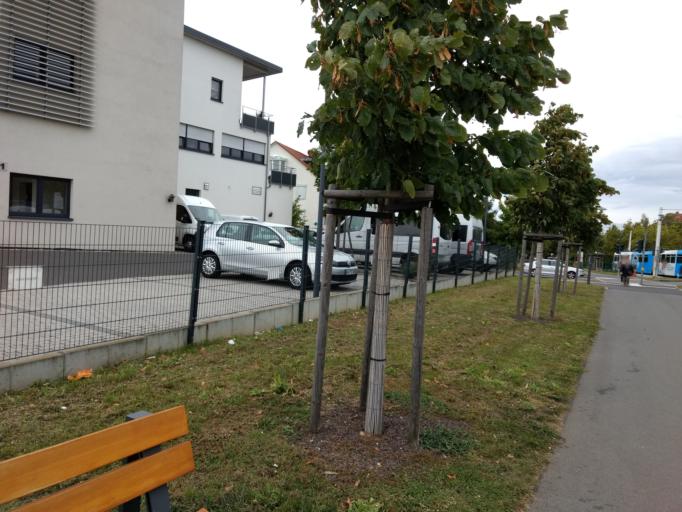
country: DE
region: Bavaria
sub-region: Regierungsbezirk Unterfranken
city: Randersacker
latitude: 49.7383
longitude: 9.9597
